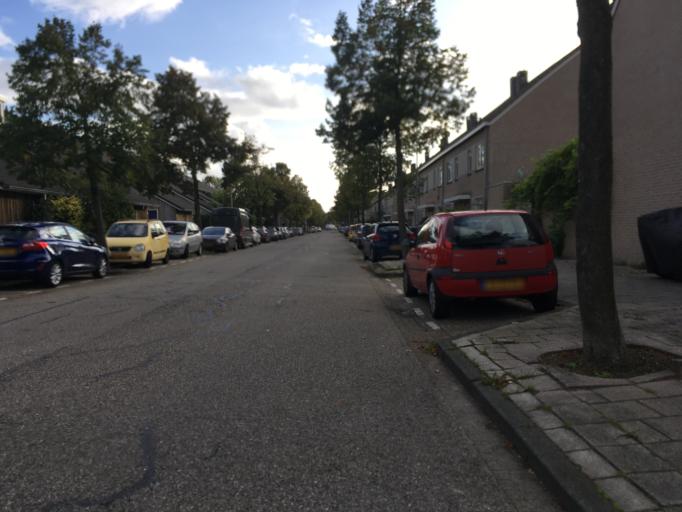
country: NL
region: North Holland
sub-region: Gemeente Haarlem
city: Haarlem
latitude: 52.3800
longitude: 4.6729
